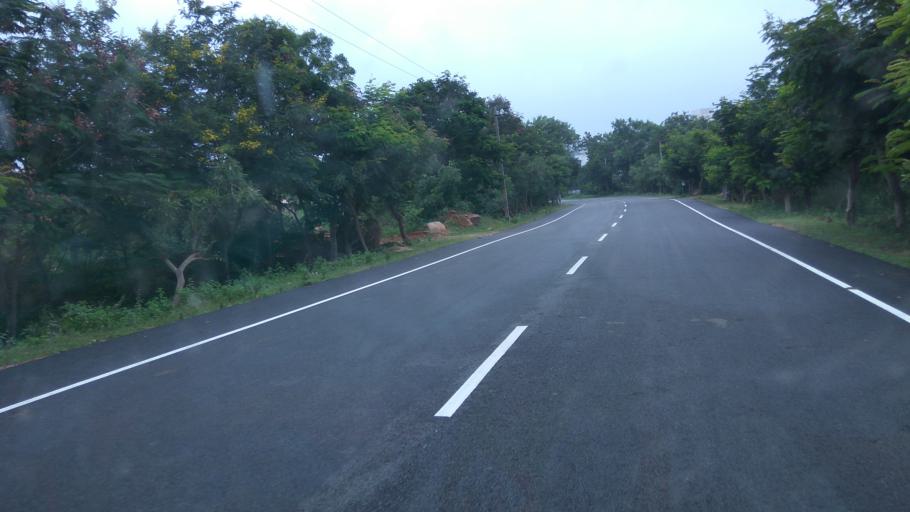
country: IN
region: Telangana
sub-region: Rangareddi
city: Ghatkesar
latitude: 17.5390
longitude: 78.6768
